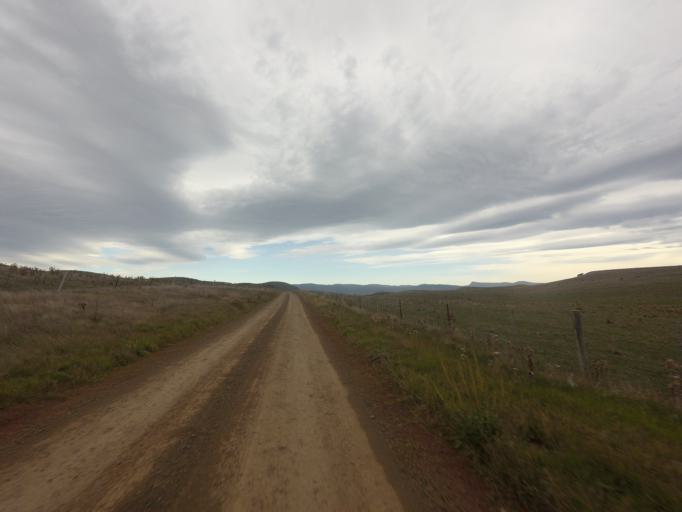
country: AU
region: Tasmania
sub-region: Derwent Valley
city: New Norfolk
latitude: -42.4360
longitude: 146.8070
